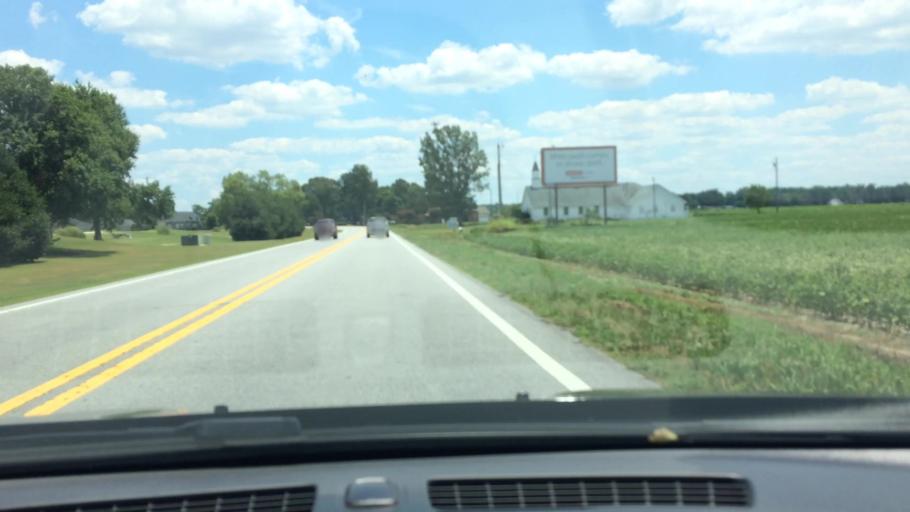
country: US
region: North Carolina
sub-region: Pitt County
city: Summerfield
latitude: 35.6372
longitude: -77.4508
